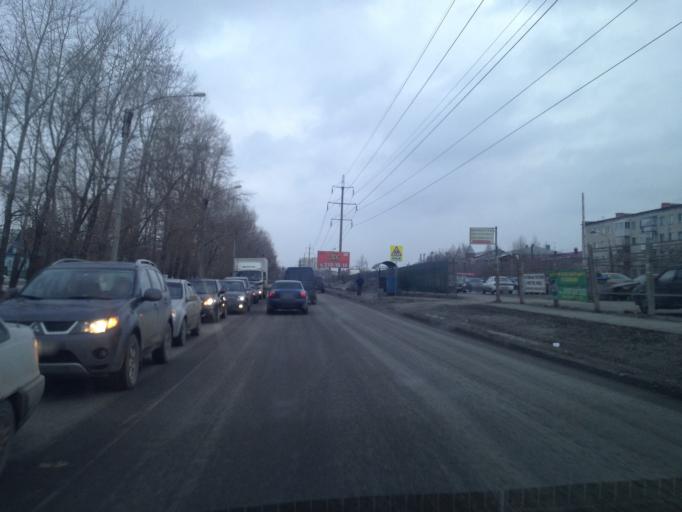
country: RU
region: Sverdlovsk
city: Sovkhoznyy
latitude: 56.7694
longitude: 60.5953
